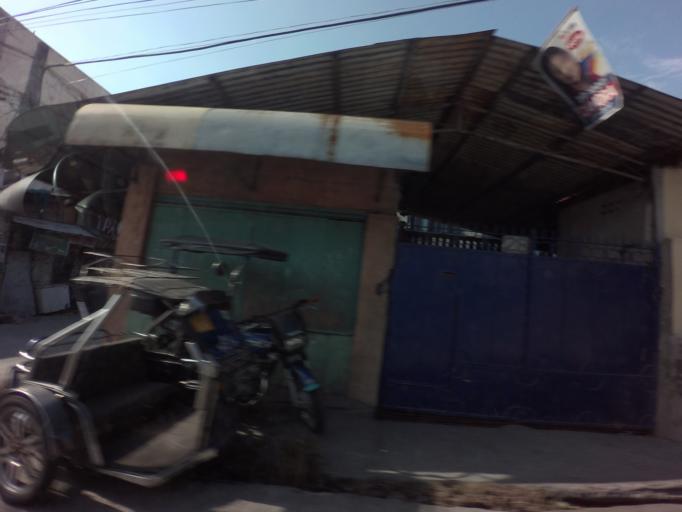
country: PH
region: Calabarzon
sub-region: Province of Rizal
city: Taguig
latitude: 14.4971
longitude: 121.0581
